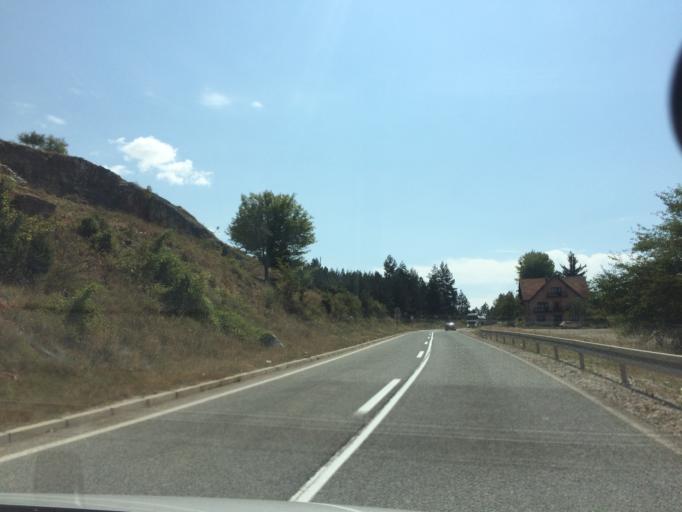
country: RS
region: Central Serbia
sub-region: Zlatiborski Okrug
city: Nova Varos
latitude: 43.5426
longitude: 19.7877
